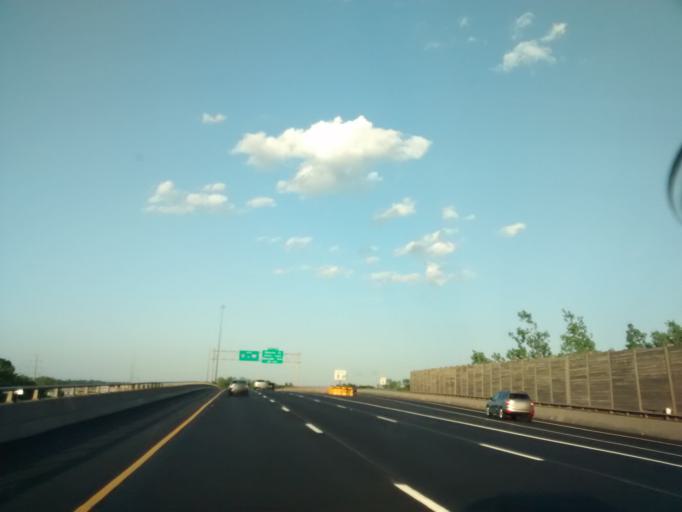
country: US
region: Connecticut
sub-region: Hartford County
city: East Hartford
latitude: 41.7632
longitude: -72.6388
